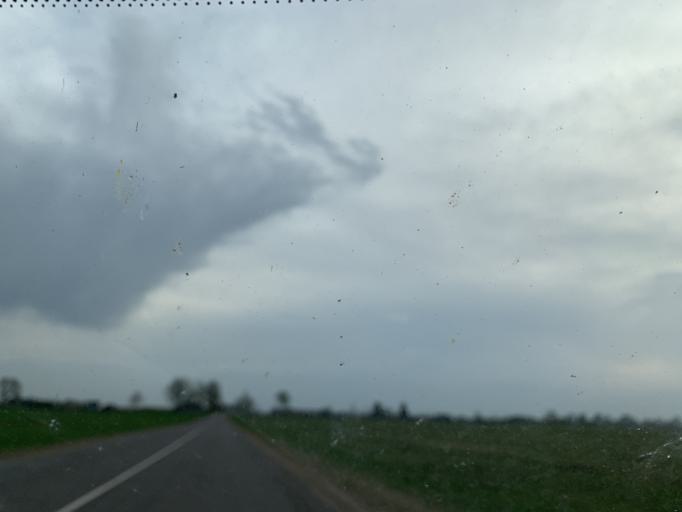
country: BY
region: Minsk
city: Kapyl'
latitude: 53.2976
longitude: 27.0381
